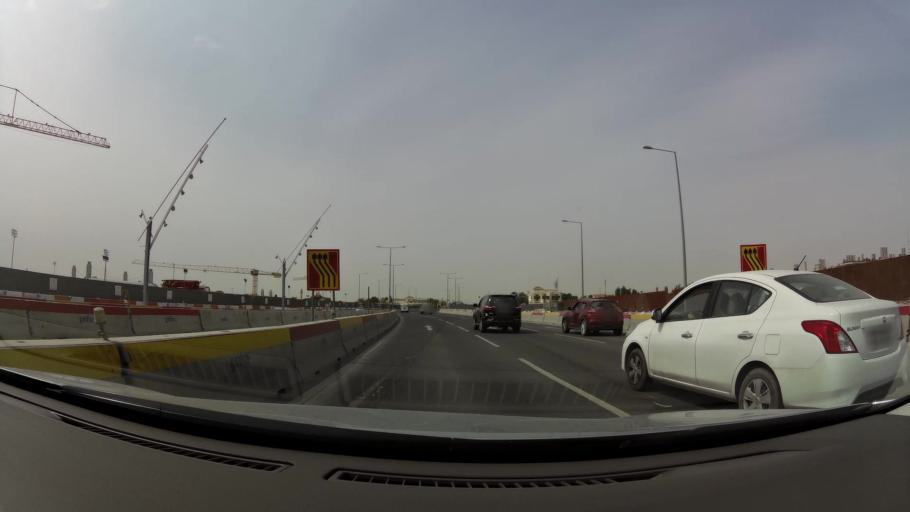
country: QA
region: Baladiyat ad Dawhah
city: Doha
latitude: 25.2738
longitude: 51.4860
